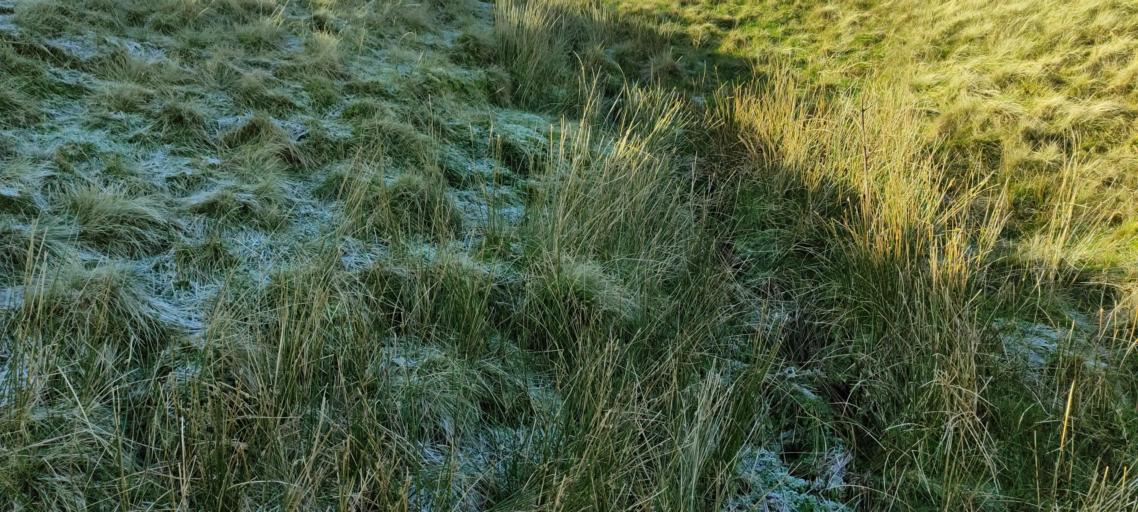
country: GB
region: England
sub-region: Cumbria
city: Sedbergh
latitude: 54.3986
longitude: -2.5548
